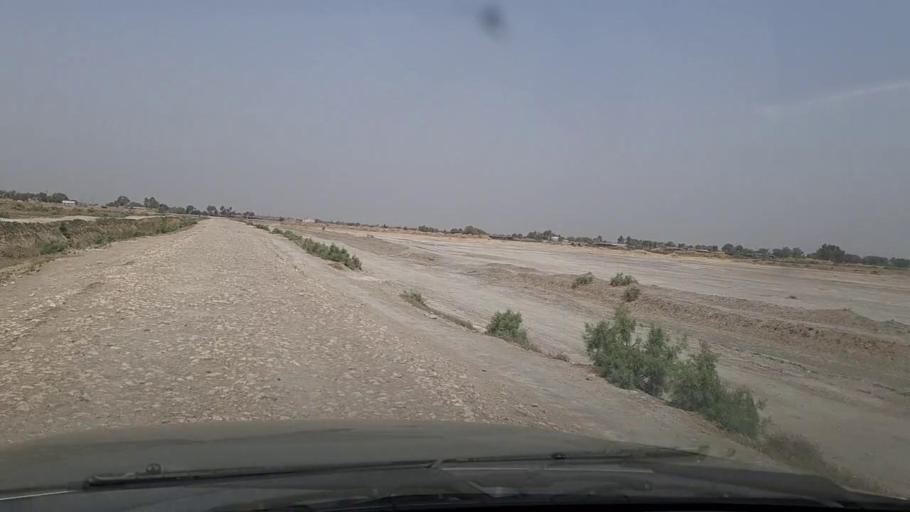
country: PK
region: Balochistan
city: Sohbatpur
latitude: 28.4132
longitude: 68.6929
